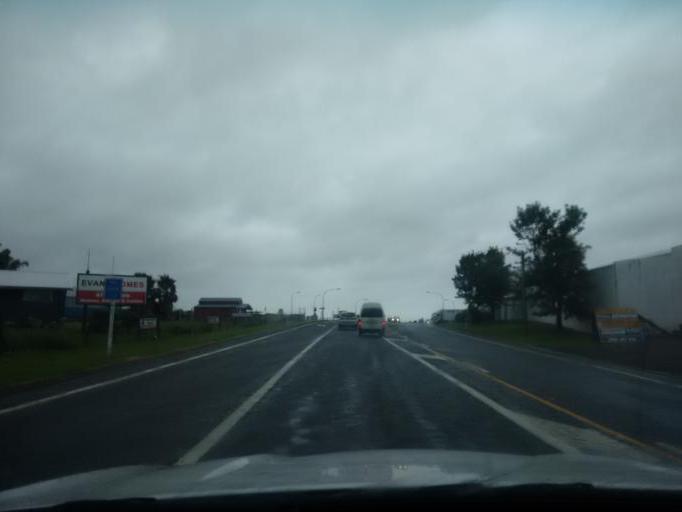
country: NZ
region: Waikato
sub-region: Thames-Coromandel District
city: Whitianga
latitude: -36.8337
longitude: 175.6731
